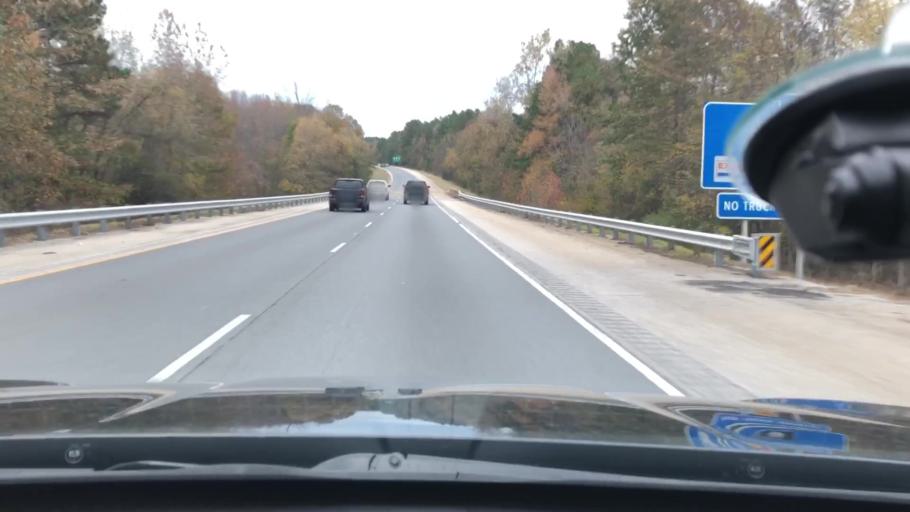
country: US
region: Arkansas
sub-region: Clark County
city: Arkadelphia
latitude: 34.0974
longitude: -93.1046
